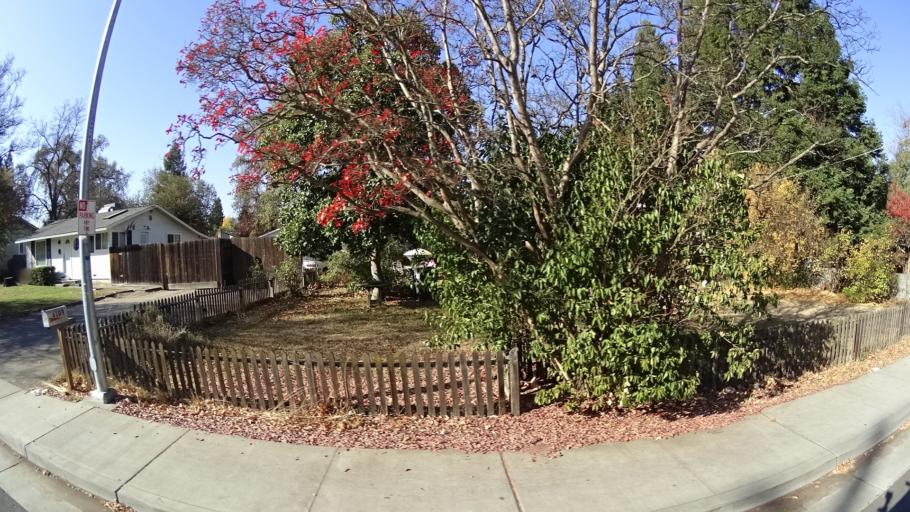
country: US
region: California
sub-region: Sacramento County
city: Citrus Heights
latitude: 38.6770
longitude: -121.2847
